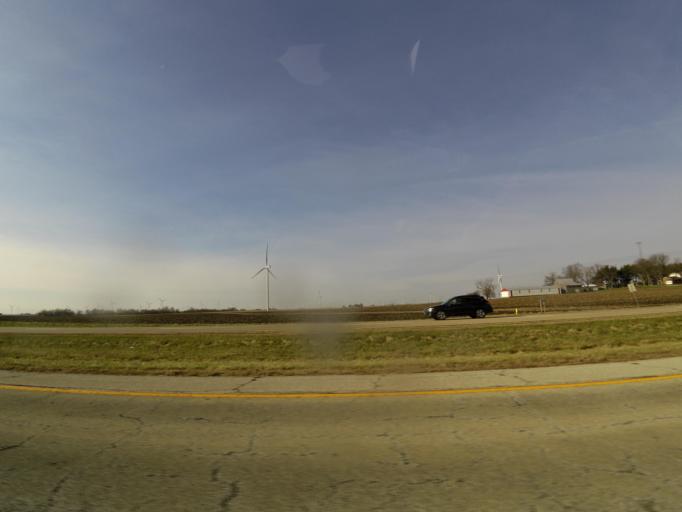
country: US
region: Illinois
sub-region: Macon County
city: Maroa
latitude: 40.0194
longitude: -88.9562
